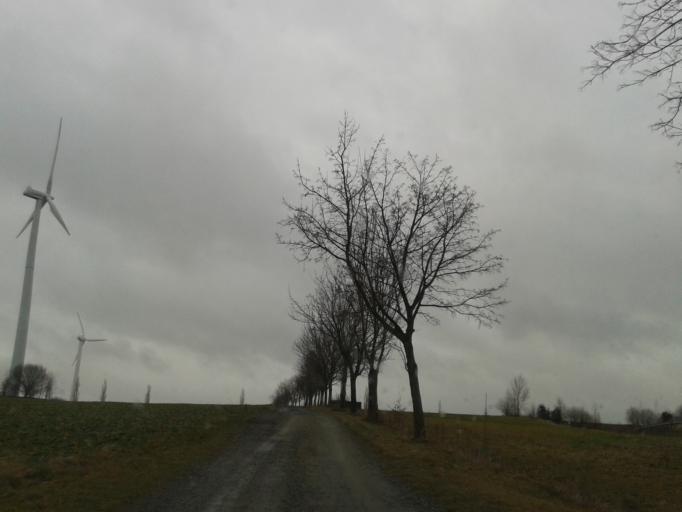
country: DE
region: Saxony
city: Neugersdorf
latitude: 50.9662
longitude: 14.6282
